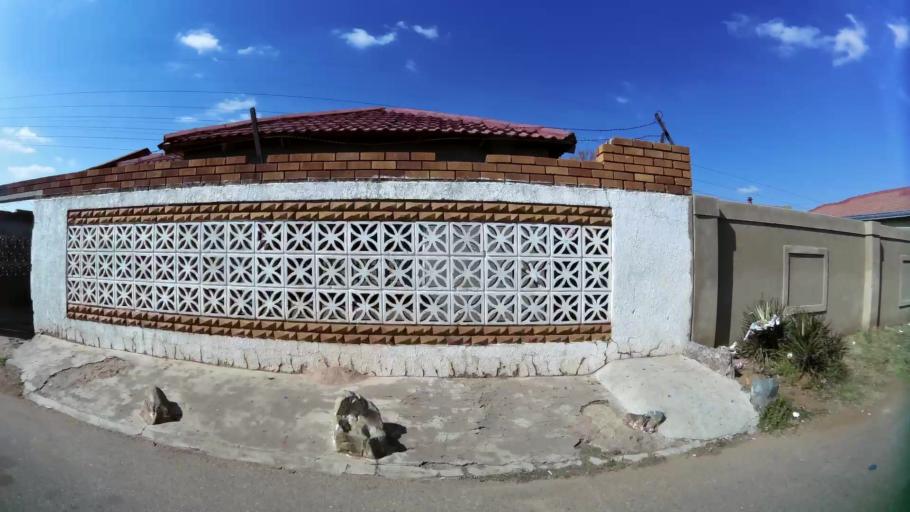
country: ZA
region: Gauteng
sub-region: City of Johannesburg Metropolitan Municipality
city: Soweto
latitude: -26.2539
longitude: 27.8905
